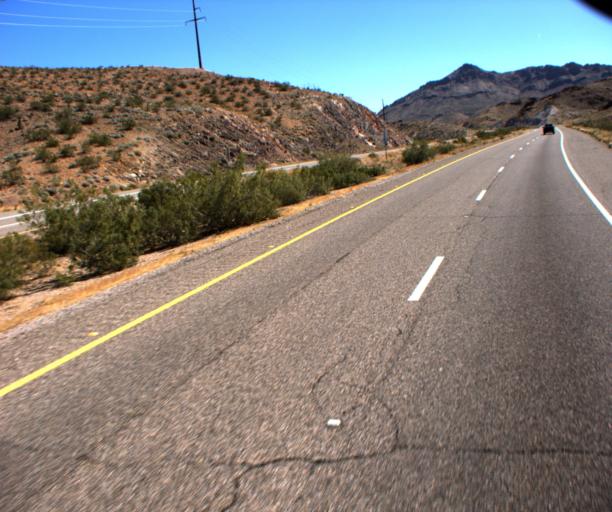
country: US
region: Nevada
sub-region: Clark County
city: Laughlin
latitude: 35.1951
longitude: -114.4367
